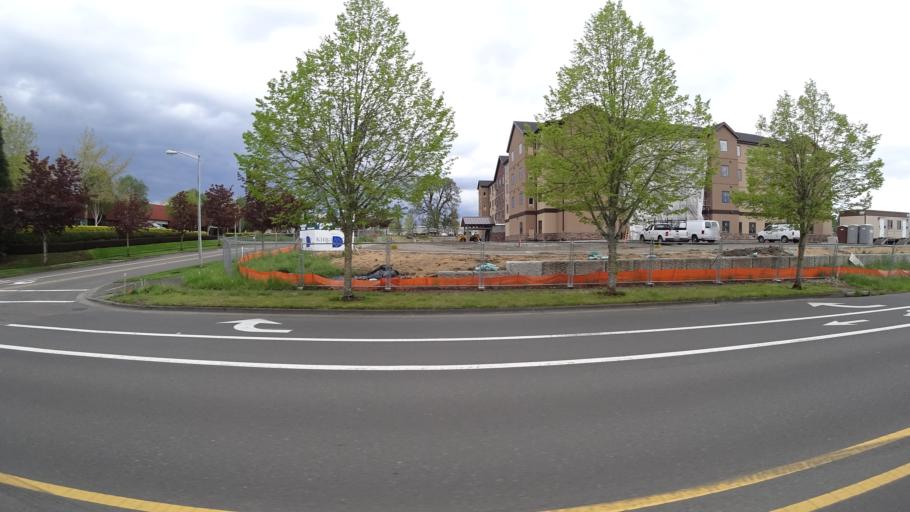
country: US
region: Oregon
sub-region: Washington County
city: Rockcreek
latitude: 45.5654
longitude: -122.9228
